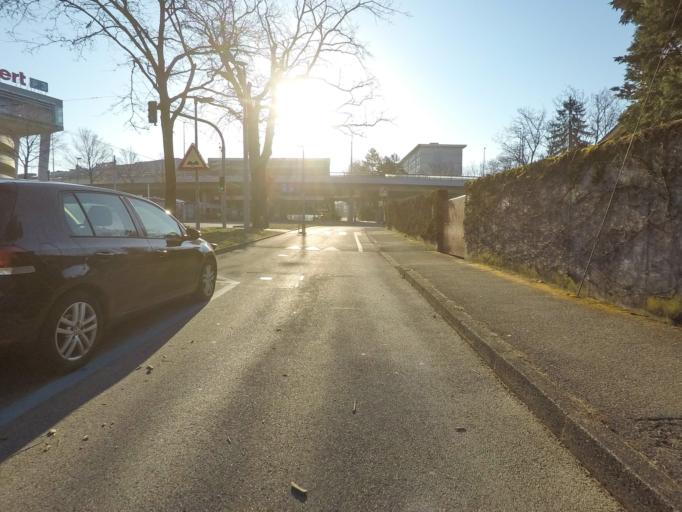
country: CH
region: Geneva
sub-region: Geneva
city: Les Avanchets
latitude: 46.2185
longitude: 6.1096
